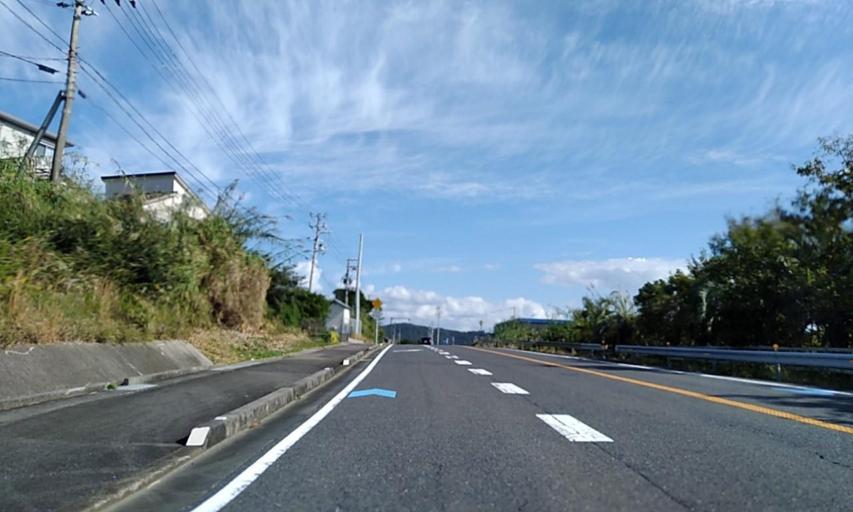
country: JP
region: Wakayama
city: Gobo
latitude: 33.8041
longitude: 135.2241
